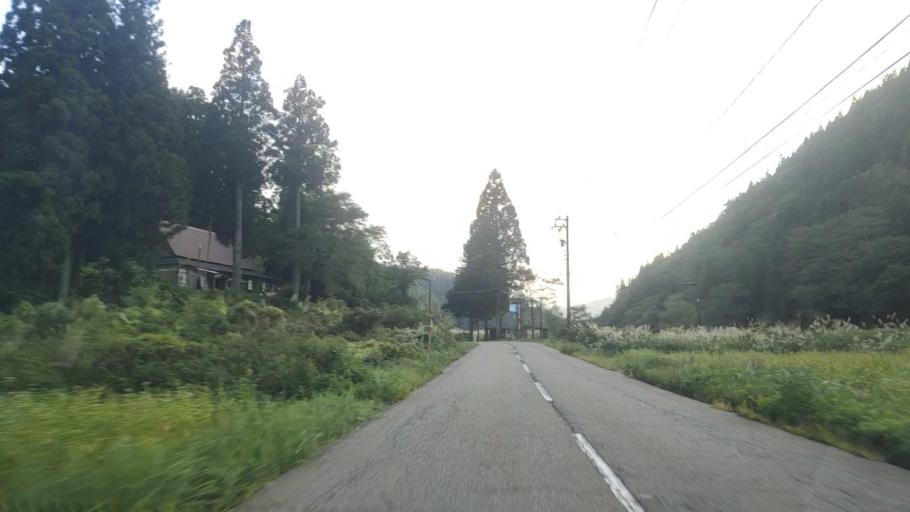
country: JP
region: Toyama
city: Yatsuomachi-higashikumisaka
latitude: 36.4710
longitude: 137.0487
